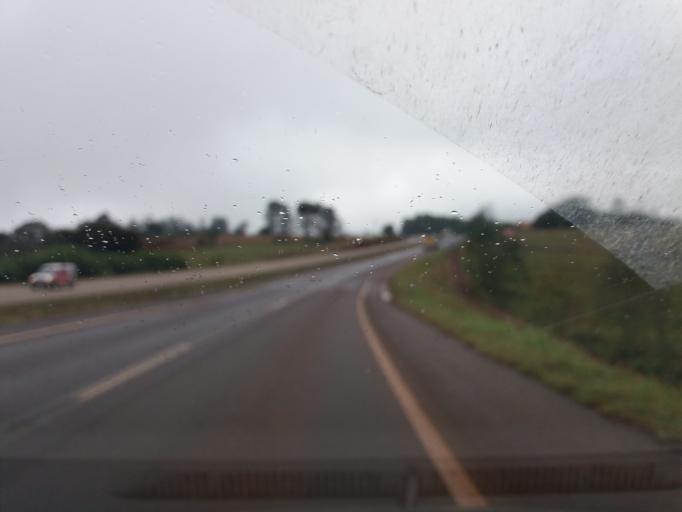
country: BR
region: Parana
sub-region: Cascavel
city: Cascavel
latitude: -25.1537
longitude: -53.5961
